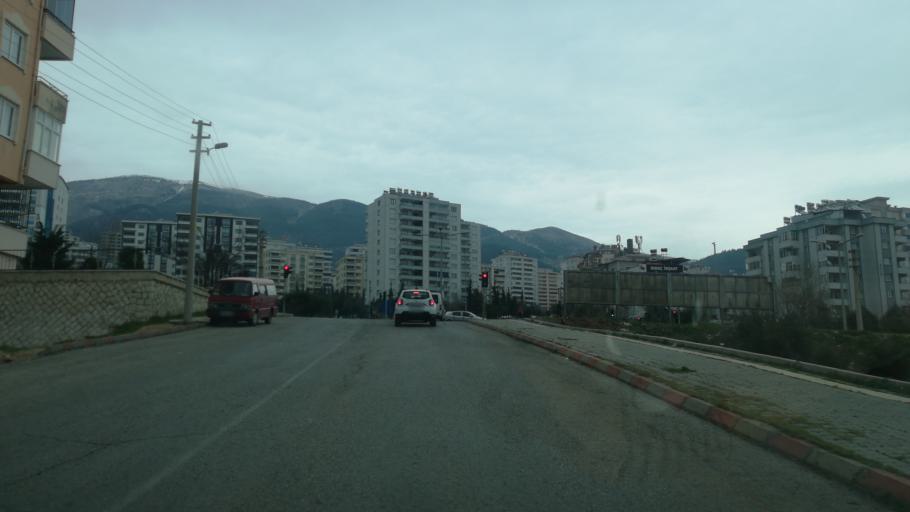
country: TR
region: Kahramanmaras
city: Kahramanmaras
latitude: 37.5946
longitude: 36.8909
